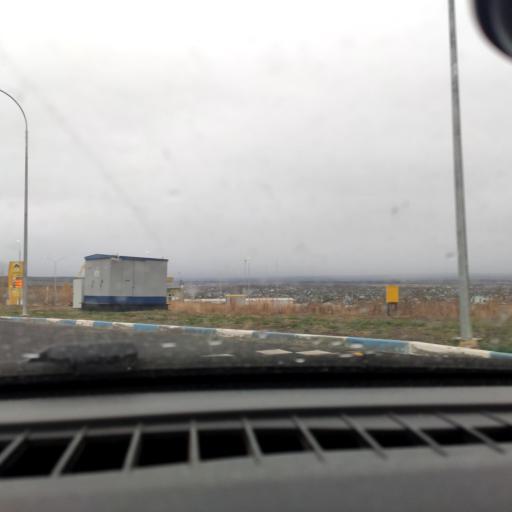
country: RU
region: Belgorod
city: Alekseyevka
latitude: 50.6442
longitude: 38.6781
